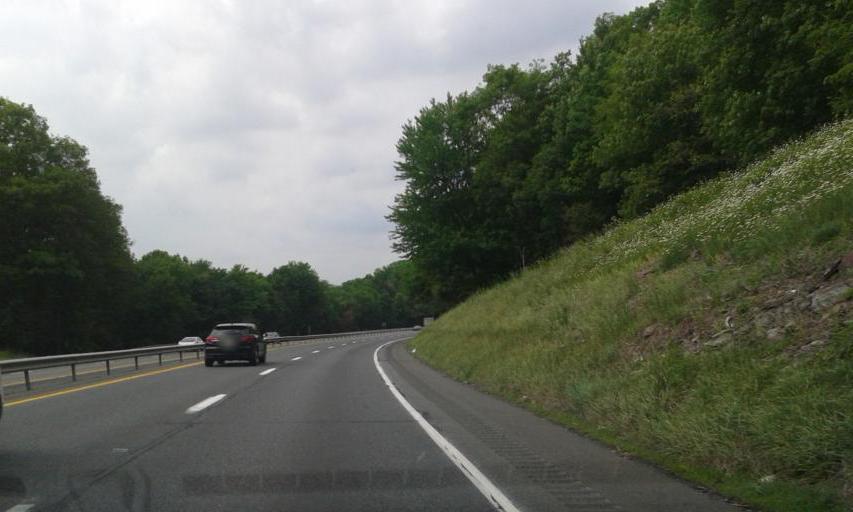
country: US
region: Pennsylvania
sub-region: Monroe County
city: Saylorsburg
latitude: 40.8732
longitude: -75.3128
